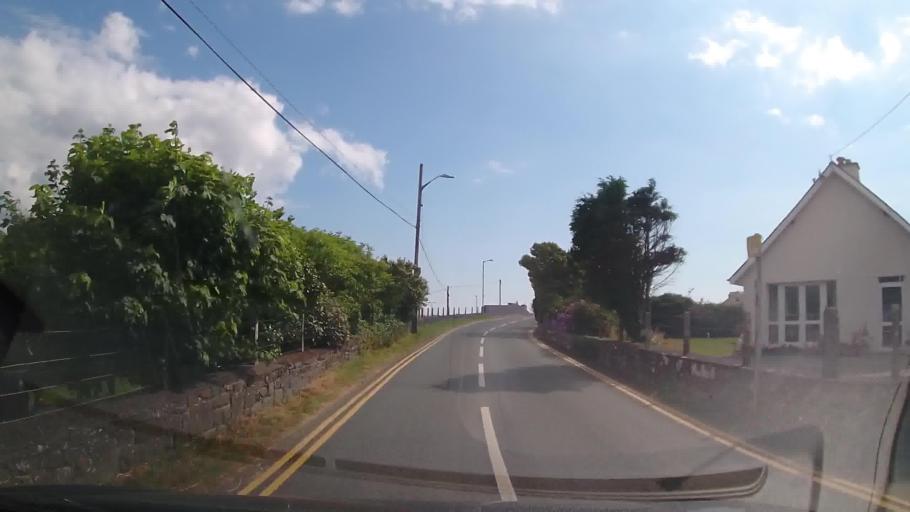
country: GB
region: Wales
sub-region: Gwynedd
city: Llanfair
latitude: 52.8372
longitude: -4.1232
